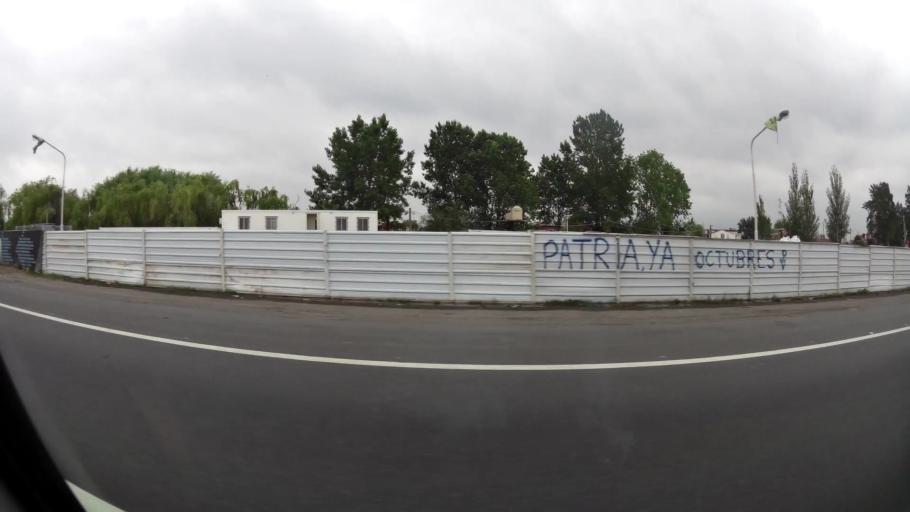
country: AR
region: Buenos Aires
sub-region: Partido de Quilmes
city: Quilmes
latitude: -34.6852
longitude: -58.3038
